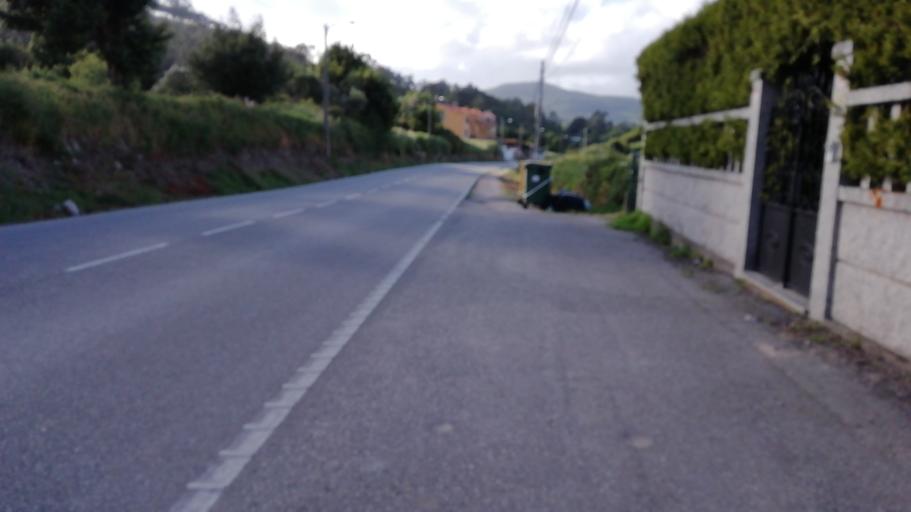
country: ES
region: Galicia
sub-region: Provincia de Pontevedra
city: A Guarda
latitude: 41.8909
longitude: -8.8579
